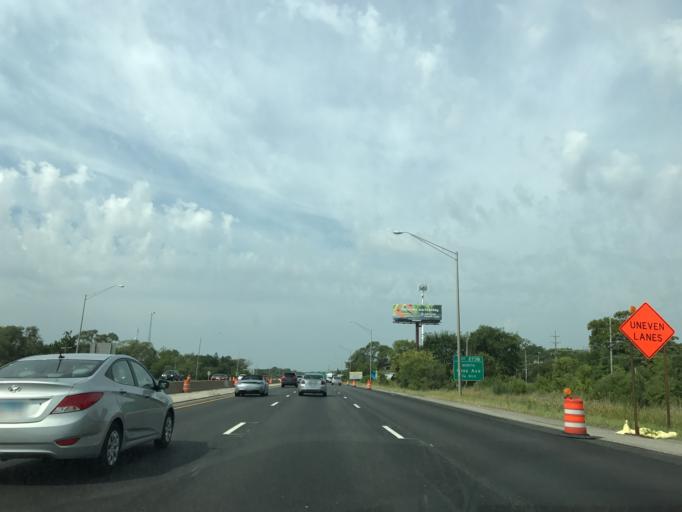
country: US
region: Illinois
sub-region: DuPage County
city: Darien
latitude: 41.7356
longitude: -87.9610
